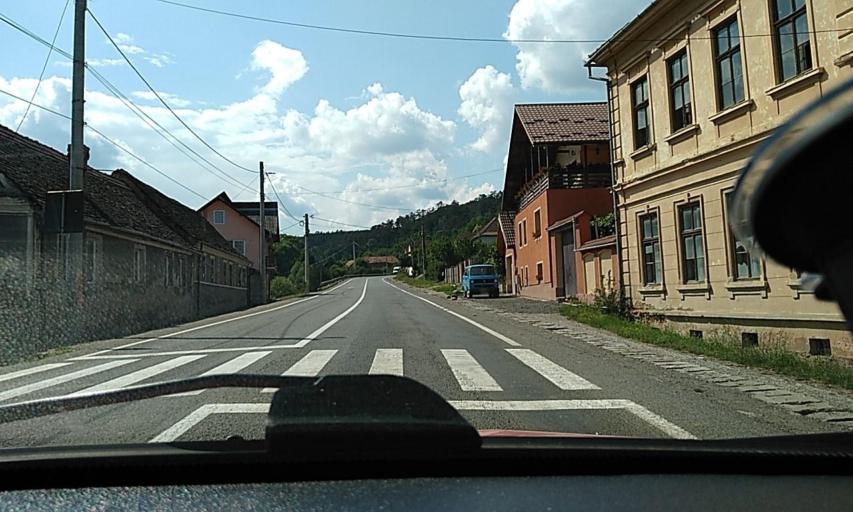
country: RO
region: Brasov
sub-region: Oras Rupea
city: Fiser
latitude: 46.0781
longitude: 25.1441
